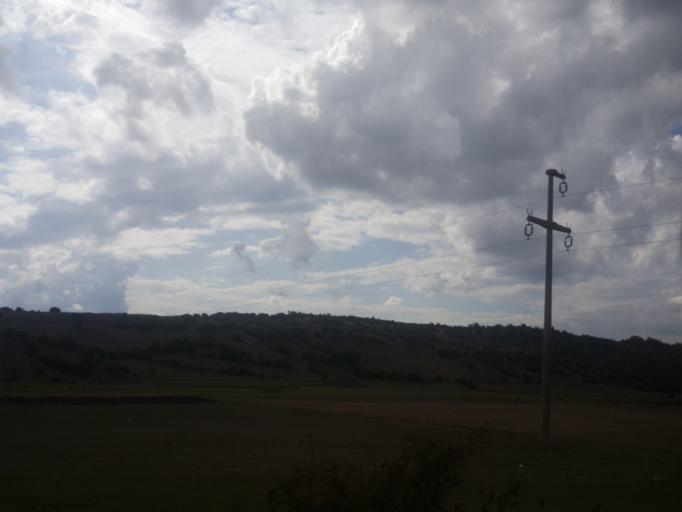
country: TR
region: Tokat
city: Bereketli
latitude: 40.5291
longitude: 37.2956
